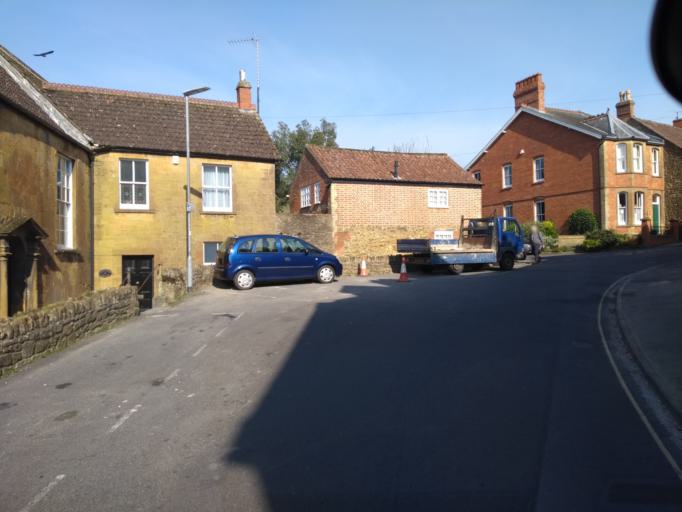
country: GB
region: England
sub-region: Somerset
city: Ilminster
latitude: 50.9271
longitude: -2.9128
